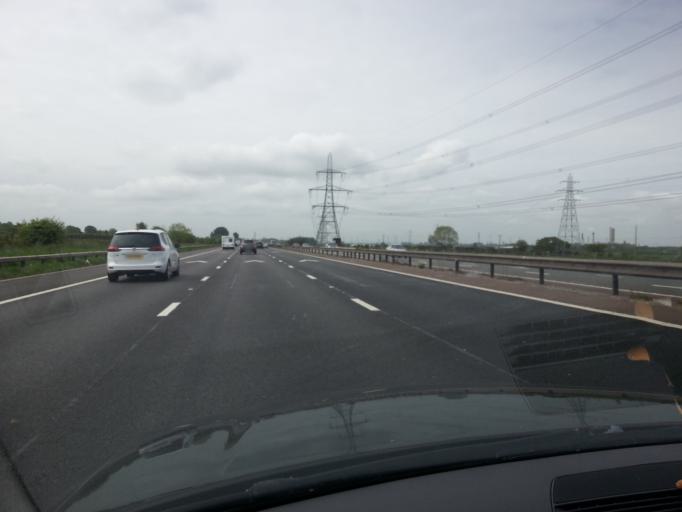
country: GB
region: England
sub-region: Cheshire West and Chester
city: Helsby
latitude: 53.2857
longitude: -2.7562
